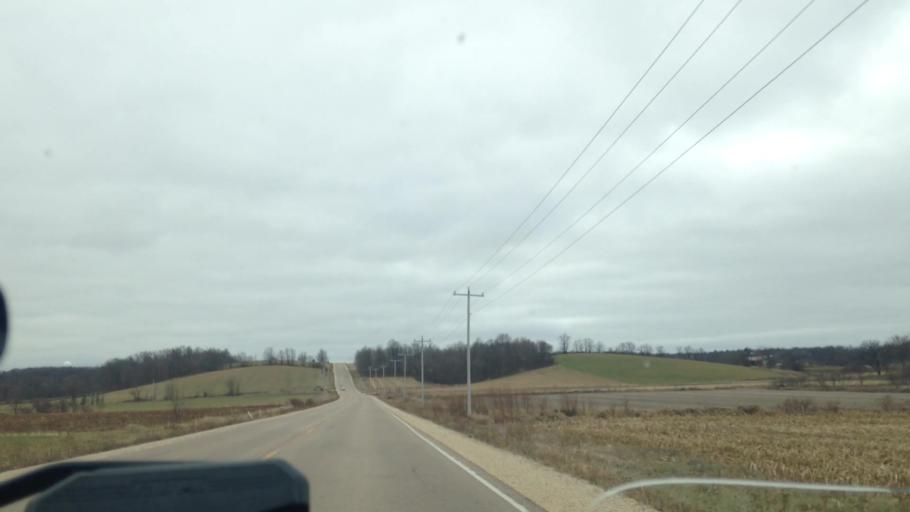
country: US
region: Wisconsin
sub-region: Dodge County
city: Mayville
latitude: 43.4666
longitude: -88.4999
